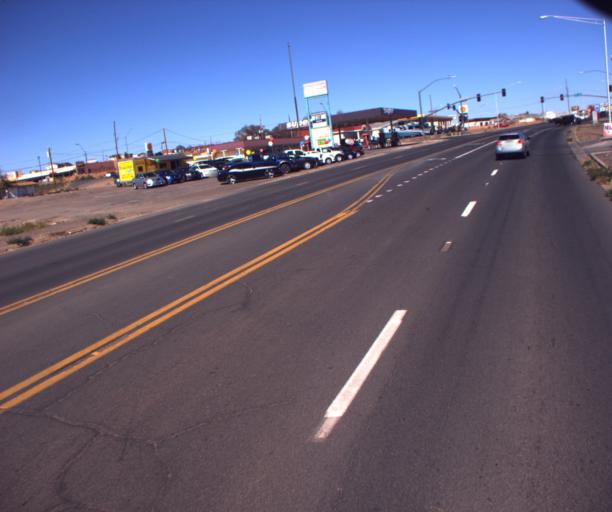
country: US
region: Arizona
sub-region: Coconino County
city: Tuba City
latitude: 36.1184
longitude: -111.2302
